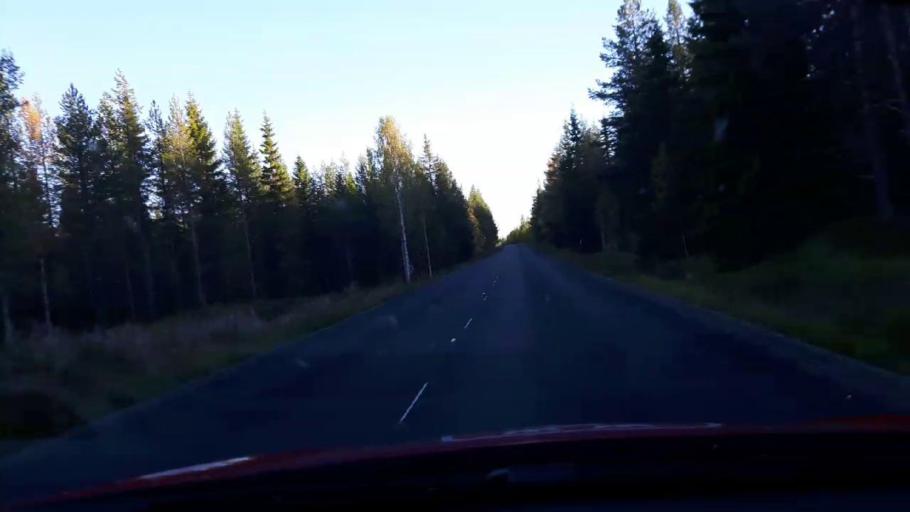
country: SE
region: Jaemtland
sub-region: OEstersunds Kommun
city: Lit
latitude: 63.4129
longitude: 14.8763
